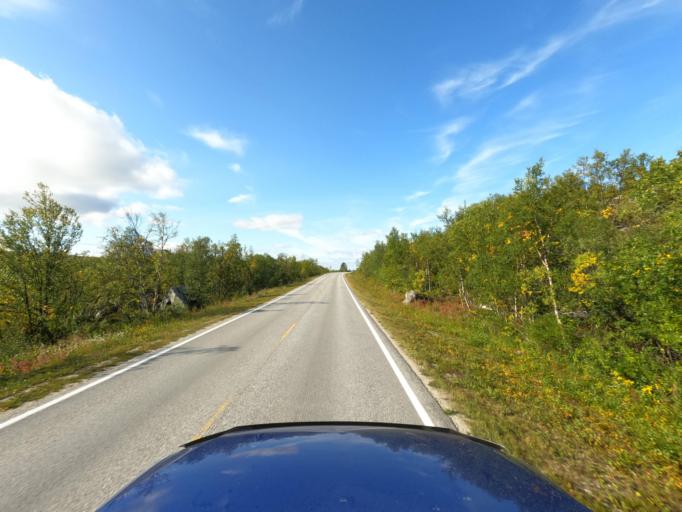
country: NO
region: Finnmark Fylke
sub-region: Porsanger
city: Lakselv
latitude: 69.7646
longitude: 25.1841
